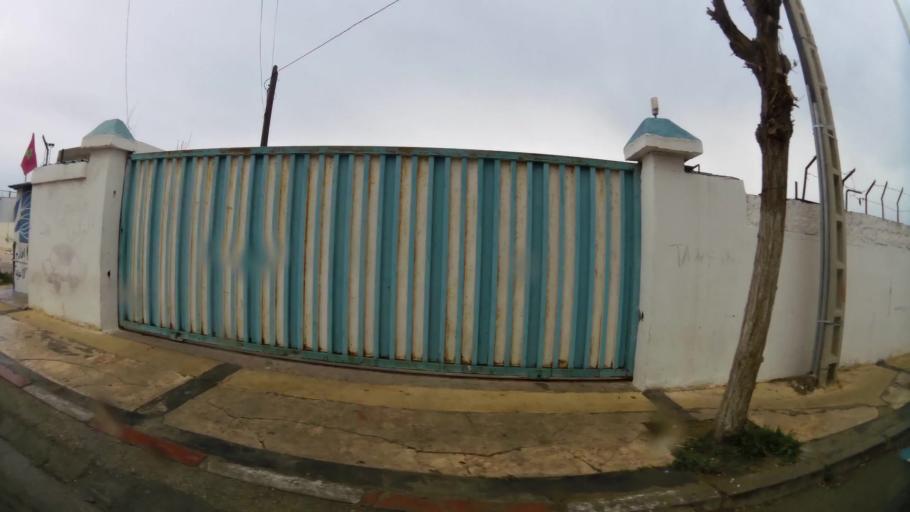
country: MA
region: Tanger-Tetouan
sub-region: Tetouan
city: Martil
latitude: 35.6194
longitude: -5.2769
